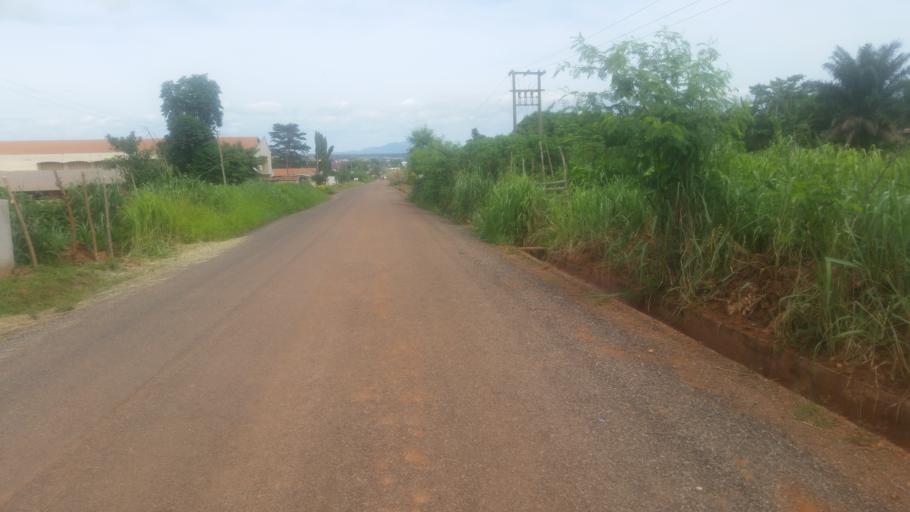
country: GH
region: Brong-Ahafo
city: Sunyani
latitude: 7.3354
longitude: -2.3455
